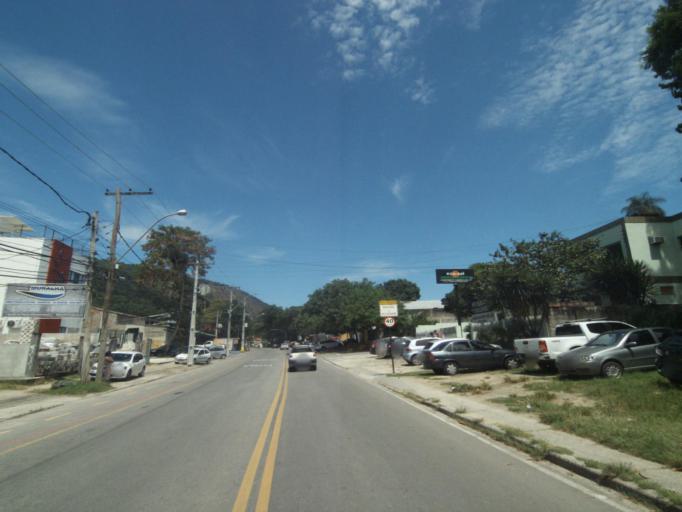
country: BR
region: Rio de Janeiro
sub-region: Niteroi
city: Niteroi
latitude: -22.9498
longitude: -43.0248
